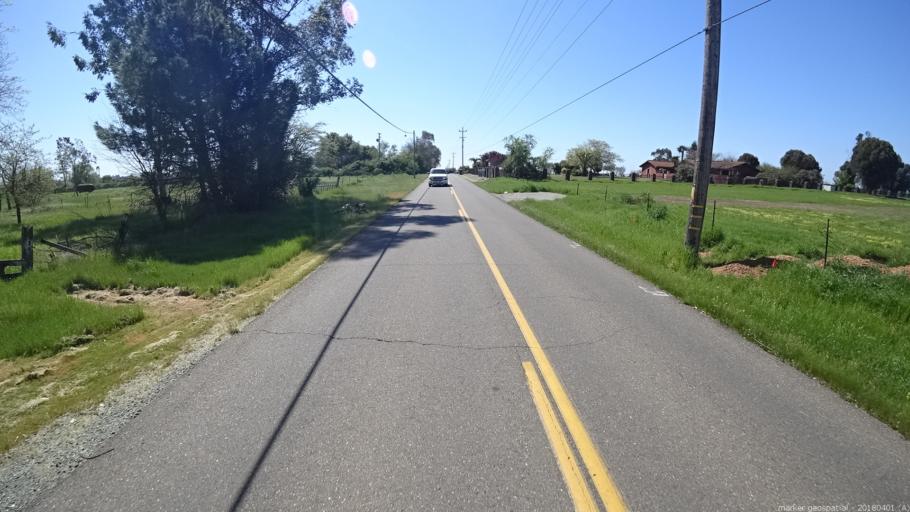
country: US
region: California
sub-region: Sacramento County
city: Wilton
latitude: 38.3751
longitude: -121.2421
